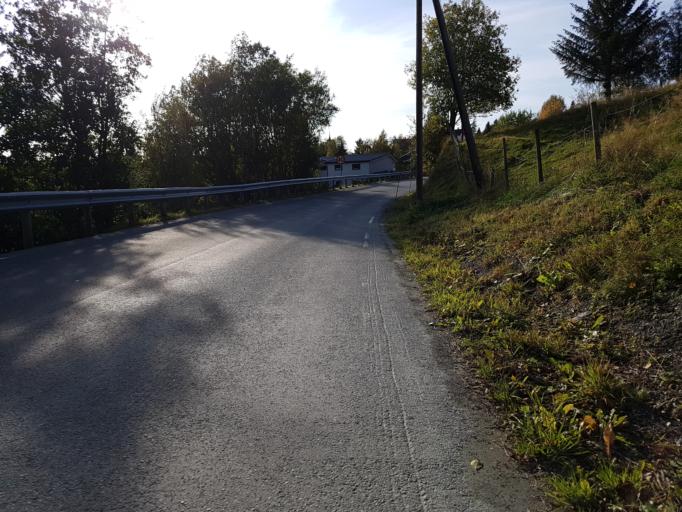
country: NO
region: Sor-Trondelag
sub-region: Klaebu
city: Klaebu
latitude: 63.3502
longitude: 10.4931
